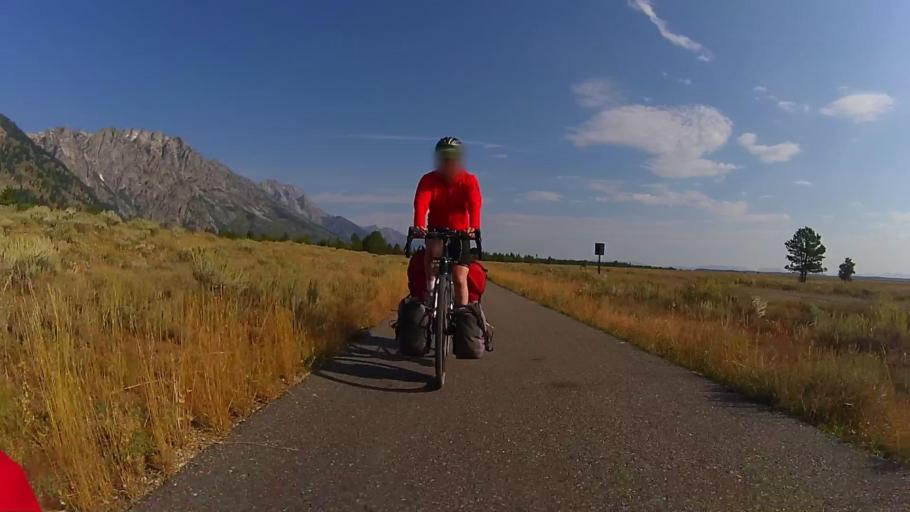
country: US
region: Wyoming
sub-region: Teton County
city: Moose Wilson Road
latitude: 43.7426
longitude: -110.7248
